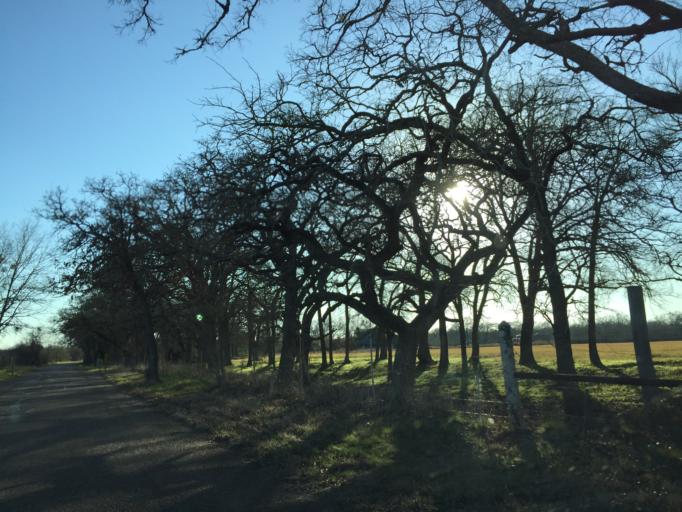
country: US
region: Texas
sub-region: Bastrop County
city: Elgin
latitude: 30.3733
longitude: -97.3168
